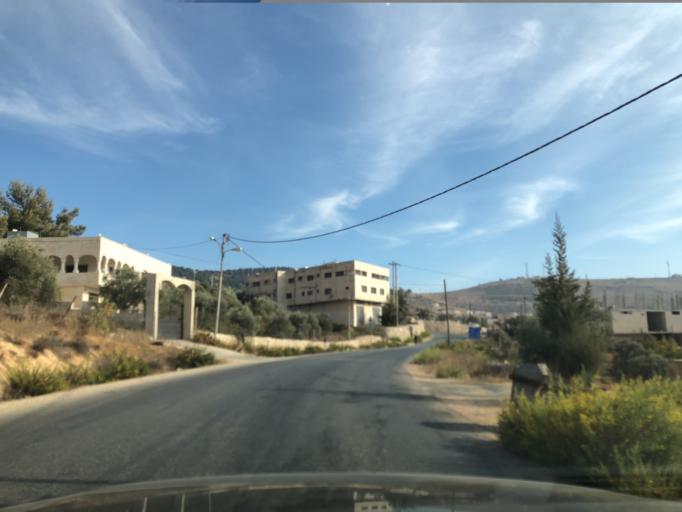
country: JO
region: Irbid
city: `Anjarah
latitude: 32.3162
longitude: 35.7710
